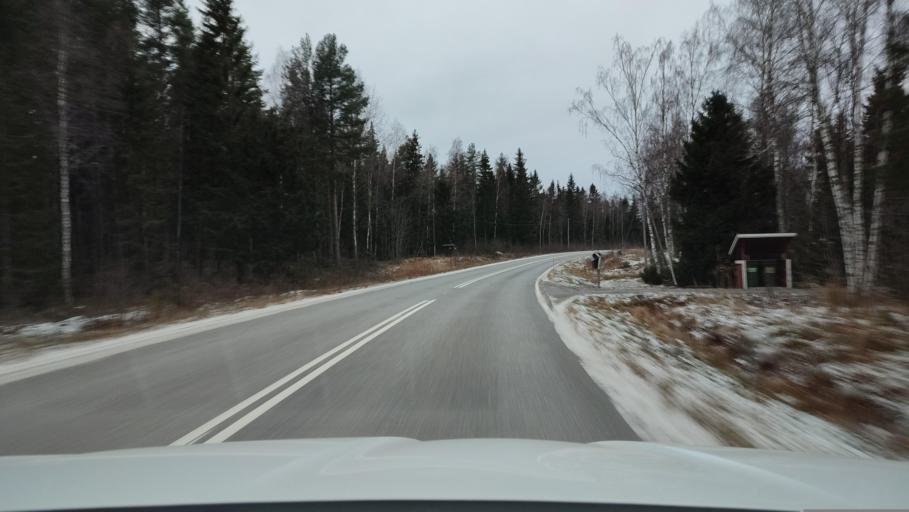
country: FI
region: Ostrobothnia
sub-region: Vaasa
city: Replot
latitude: 63.2662
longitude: 21.3502
